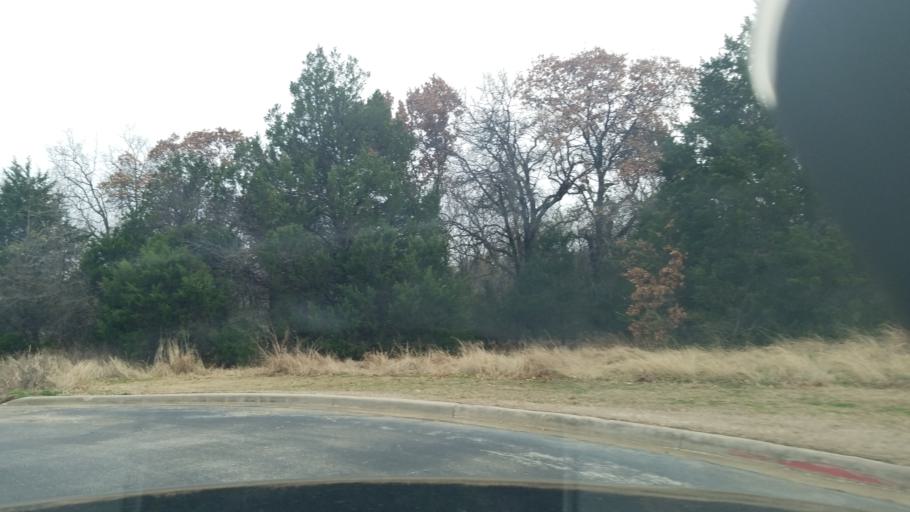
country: US
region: Texas
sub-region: Denton County
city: Corinth
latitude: 33.1511
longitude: -97.0507
